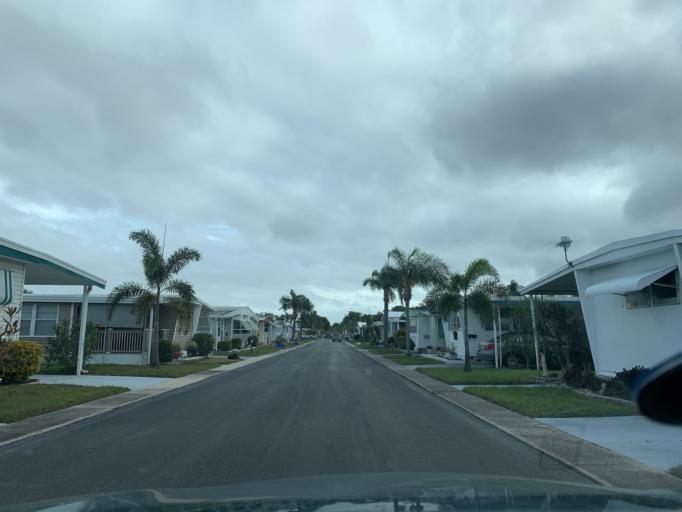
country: US
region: Florida
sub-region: Pinellas County
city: Largo
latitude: 27.8862
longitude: -82.7818
